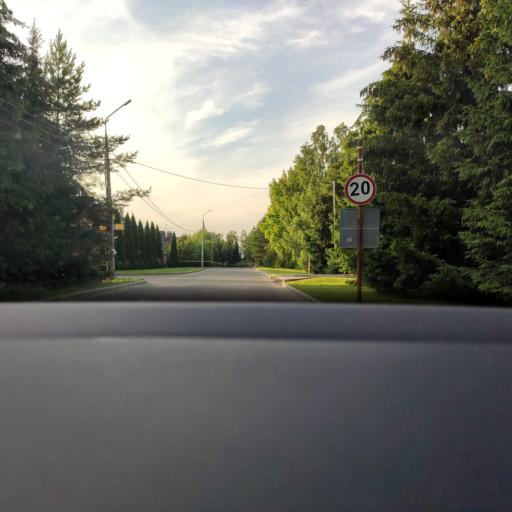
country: RU
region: Moscow
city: Lianozovo
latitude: 55.9213
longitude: 37.6059
